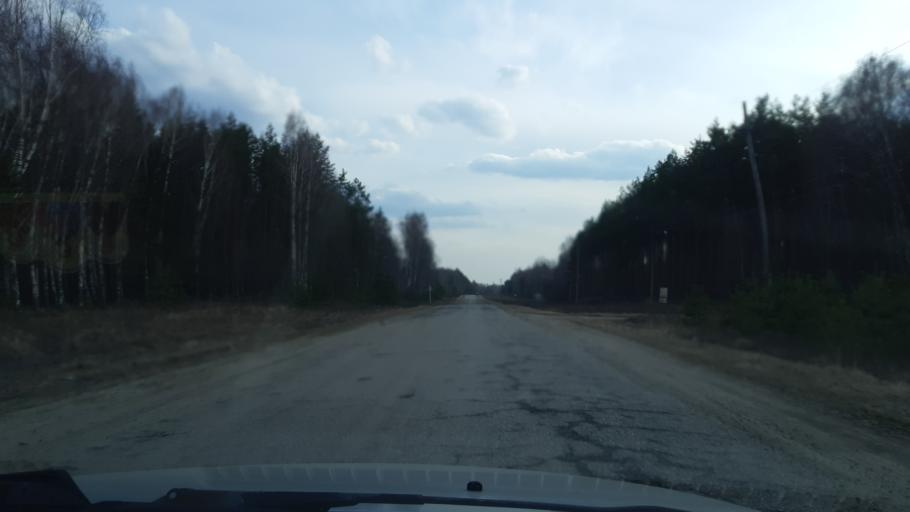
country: RU
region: Vladimir
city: Nikologory
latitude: 56.1182
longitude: 41.9858
